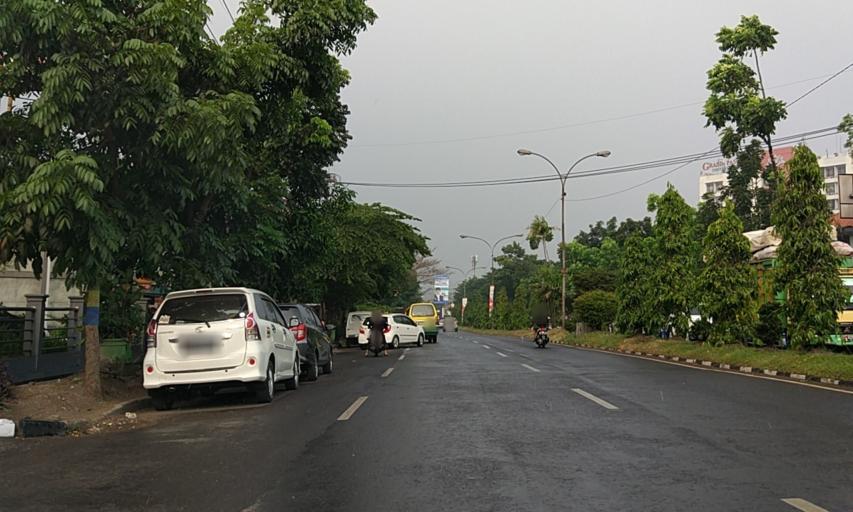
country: ID
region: West Java
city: Bandung
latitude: -6.9353
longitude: 107.5924
